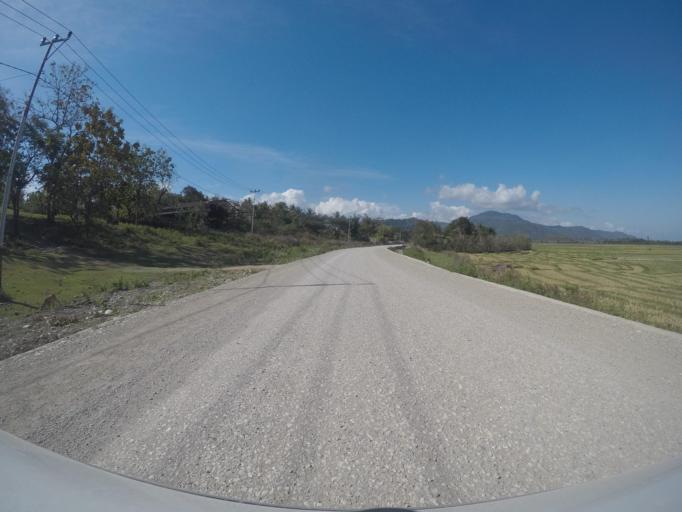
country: TL
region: Viqueque
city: Viqueque
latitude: -8.8172
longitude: 126.5336
